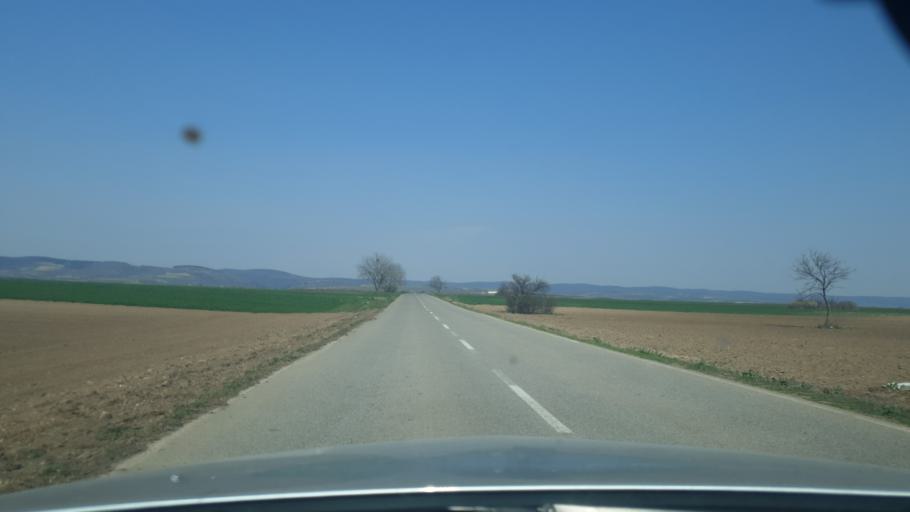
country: RS
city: Vrdnik
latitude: 45.0615
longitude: 19.7685
